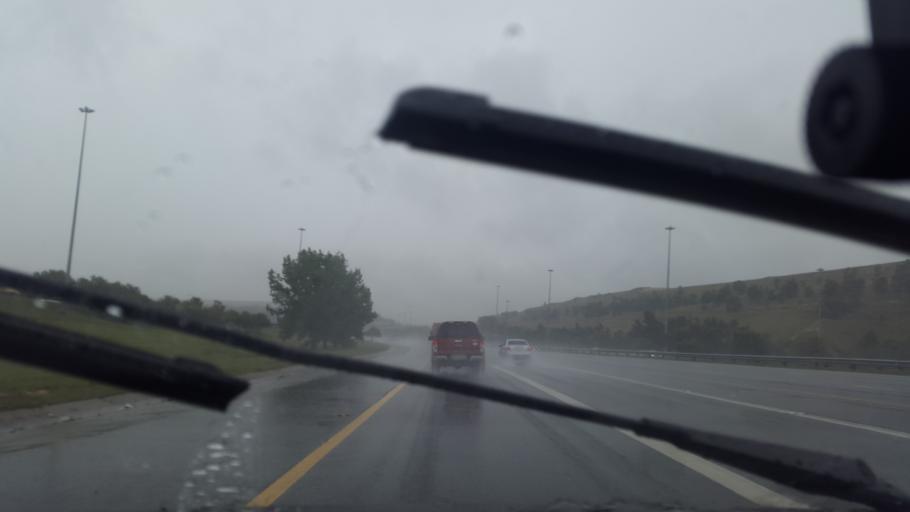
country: ZA
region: Gauteng
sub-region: City of Johannesburg Metropolitan Municipality
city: Johannesburg
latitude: -26.2490
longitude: 27.9639
